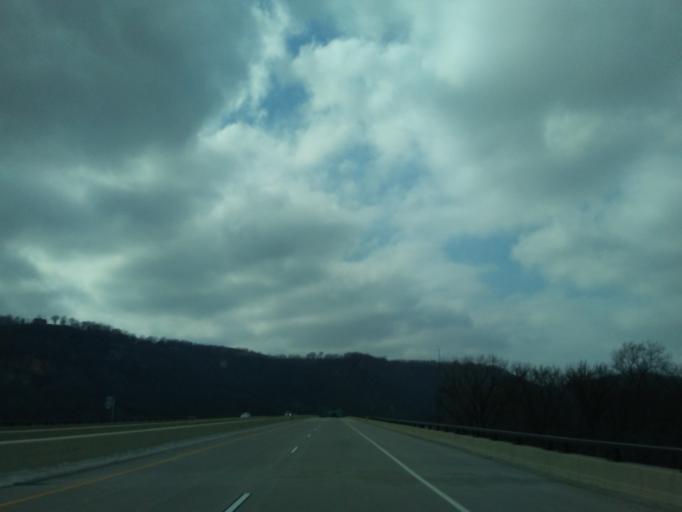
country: US
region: Minnesota
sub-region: Houston County
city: La Crescent
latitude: 43.8586
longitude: -91.2946
